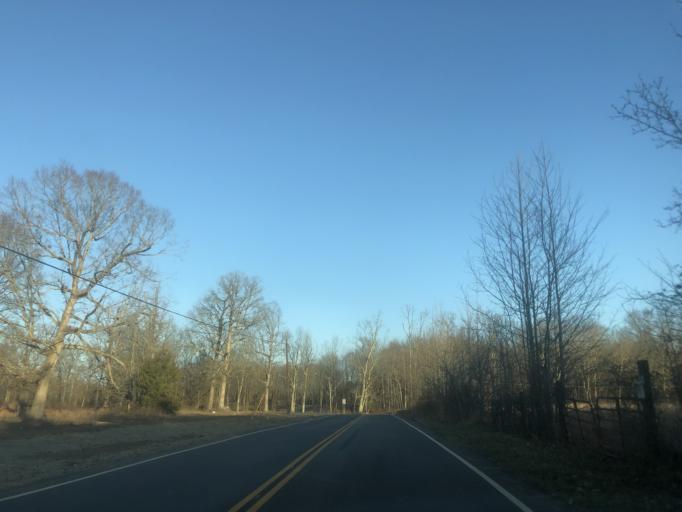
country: US
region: Tennessee
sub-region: Sumner County
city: White House
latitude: 36.4812
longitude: -86.6995
